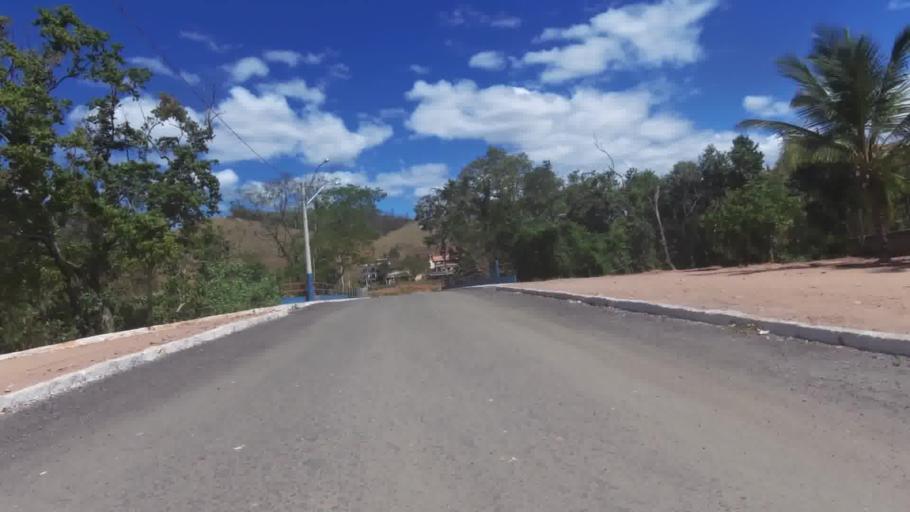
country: BR
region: Espirito Santo
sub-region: Cachoeiro De Itapemirim
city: Cachoeiro de Itapemirim
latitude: -20.9197
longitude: -41.1874
